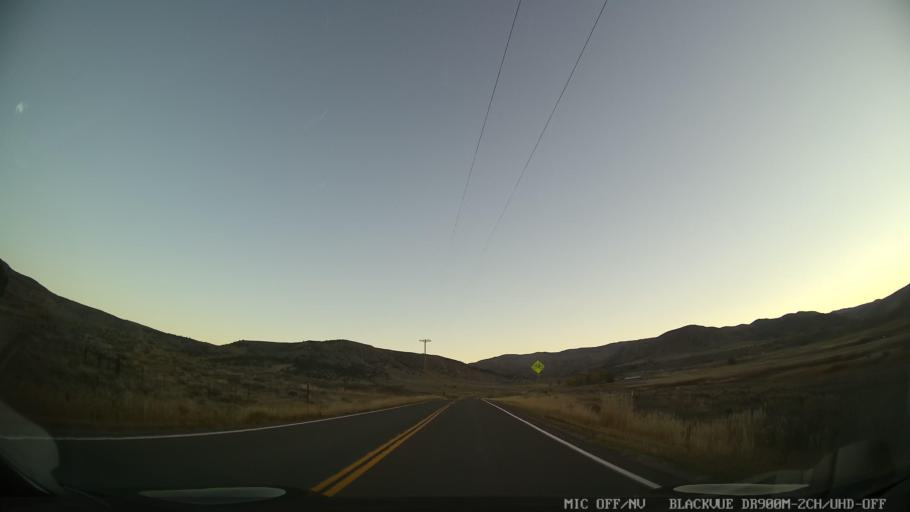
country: US
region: Colorado
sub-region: Eagle County
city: Edwards
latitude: 39.7394
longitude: -106.6786
